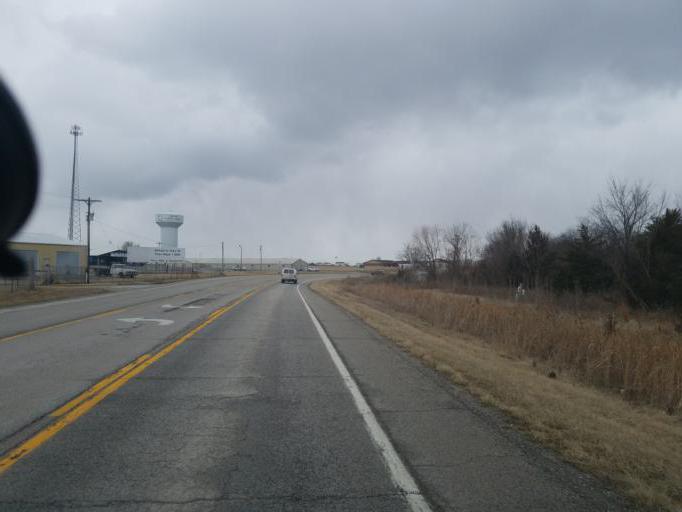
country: US
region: Missouri
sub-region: Macon County
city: Macon
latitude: 39.7646
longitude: -92.4683
